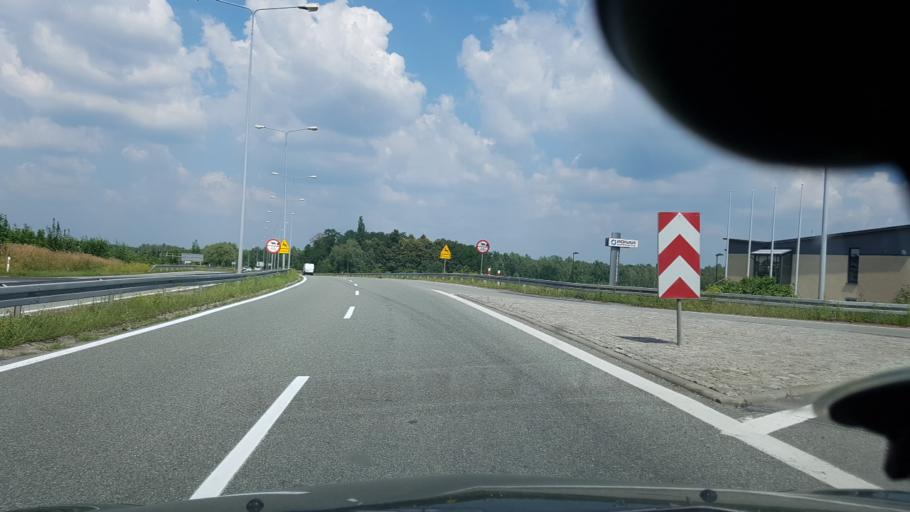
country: PL
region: Silesian Voivodeship
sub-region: Powiat mikolowski
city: Laziska Gorne
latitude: 50.1489
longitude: 18.8501
